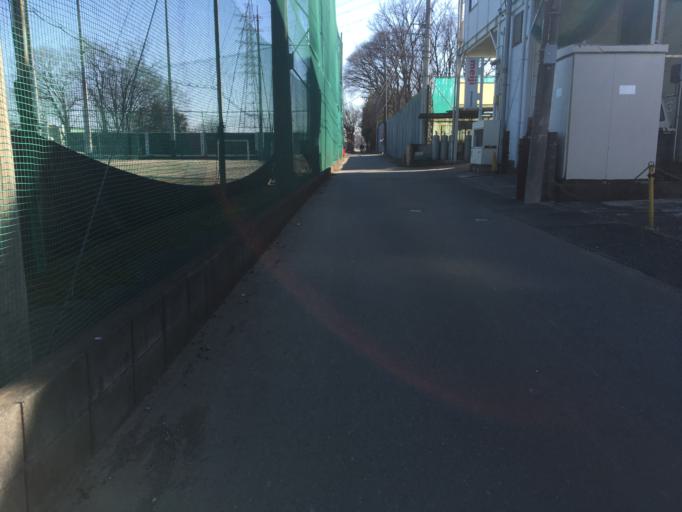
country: JP
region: Saitama
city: Oi
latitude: 35.8219
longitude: 139.5305
